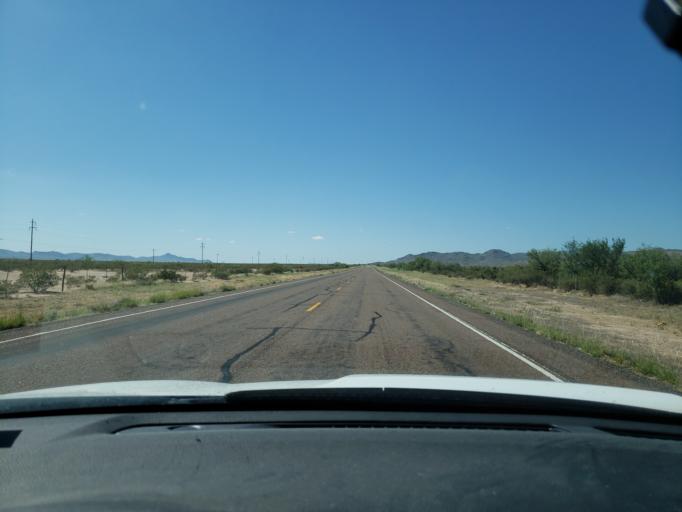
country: US
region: Texas
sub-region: Culberson County
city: Van Horn
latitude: 30.9466
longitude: -104.8125
